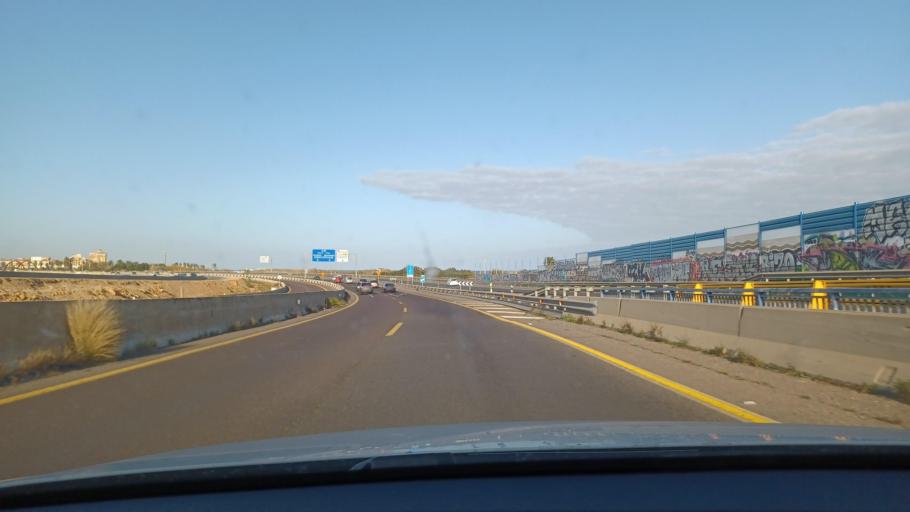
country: ES
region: Valencia
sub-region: Provincia de Valencia
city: Alboraya
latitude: 39.4953
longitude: -0.3284
